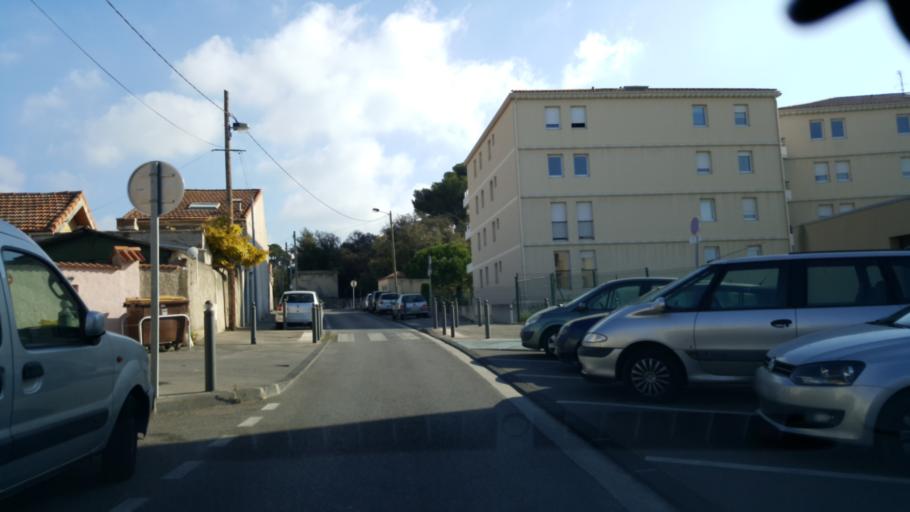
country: FR
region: Provence-Alpes-Cote d'Azur
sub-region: Departement des Bouches-du-Rhone
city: Marseille 10
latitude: 43.2657
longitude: 5.4132
